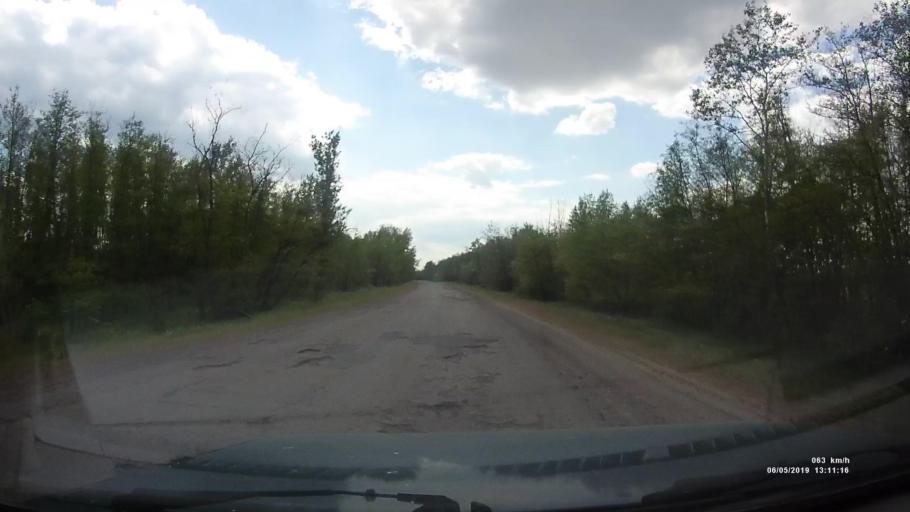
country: RU
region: Rostov
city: Ust'-Donetskiy
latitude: 47.7567
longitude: 40.9598
